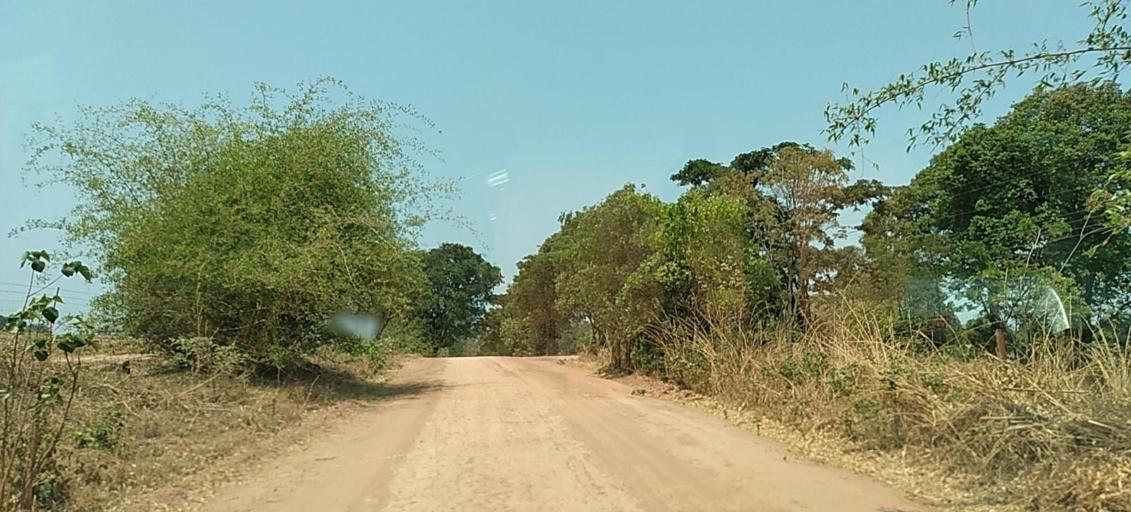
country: ZM
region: Copperbelt
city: Chambishi
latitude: -12.6257
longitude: 27.9495
